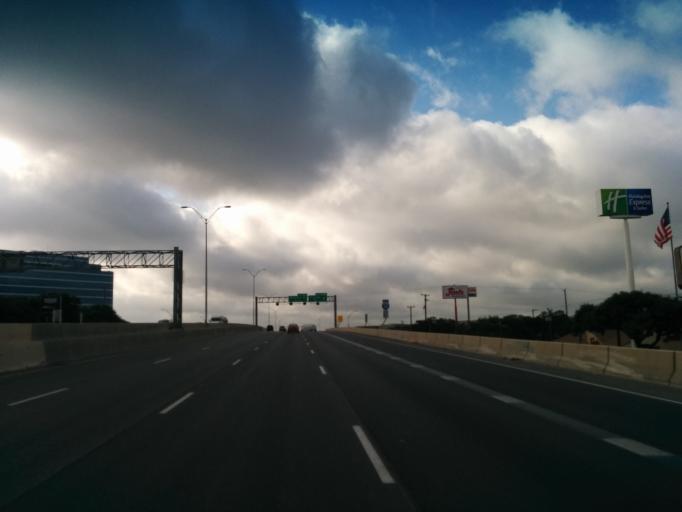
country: US
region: Texas
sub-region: Bexar County
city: Shavano Park
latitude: 29.5458
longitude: -98.5808
